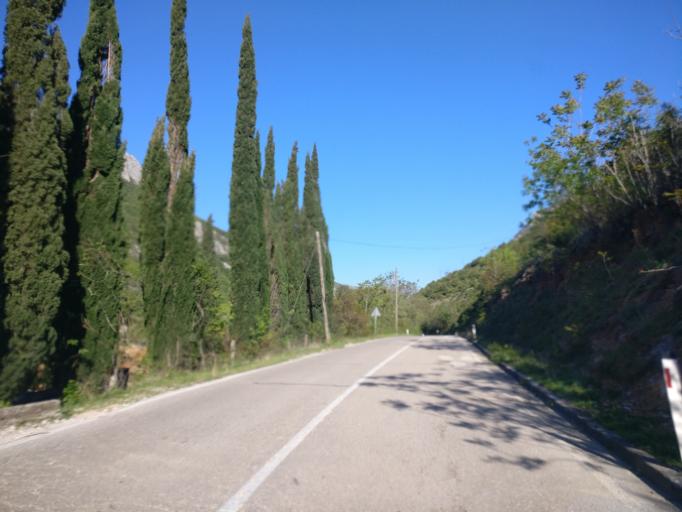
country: BA
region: Federation of Bosnia and Herzegovina
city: Stolac
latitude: 43.0727
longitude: 18.0347
